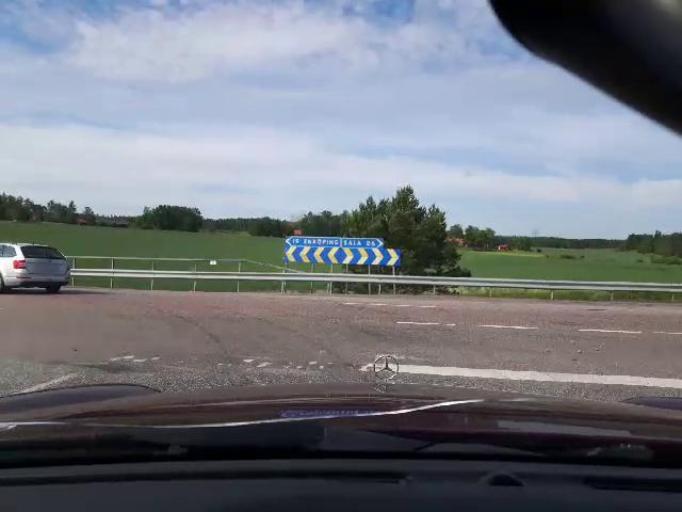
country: SE
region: Uppsala
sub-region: Enkopings Kommun
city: Irsta
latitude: 59.7699
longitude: 16.9119
